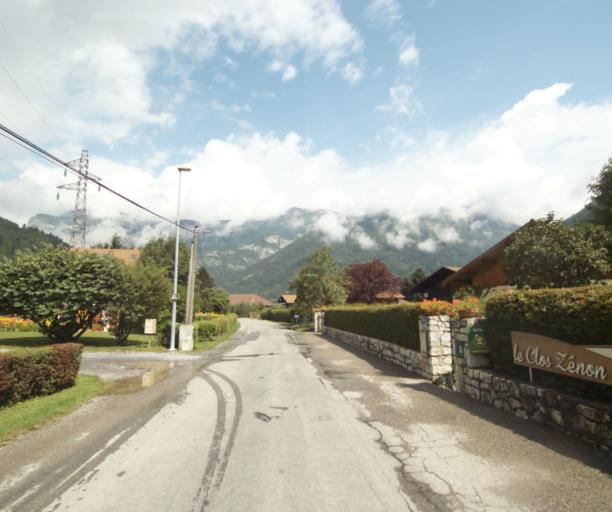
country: FR
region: Rhone-Alpes
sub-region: Departement de la Haute-Savoie
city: Thones
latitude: 45.8865
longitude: 6.3080
